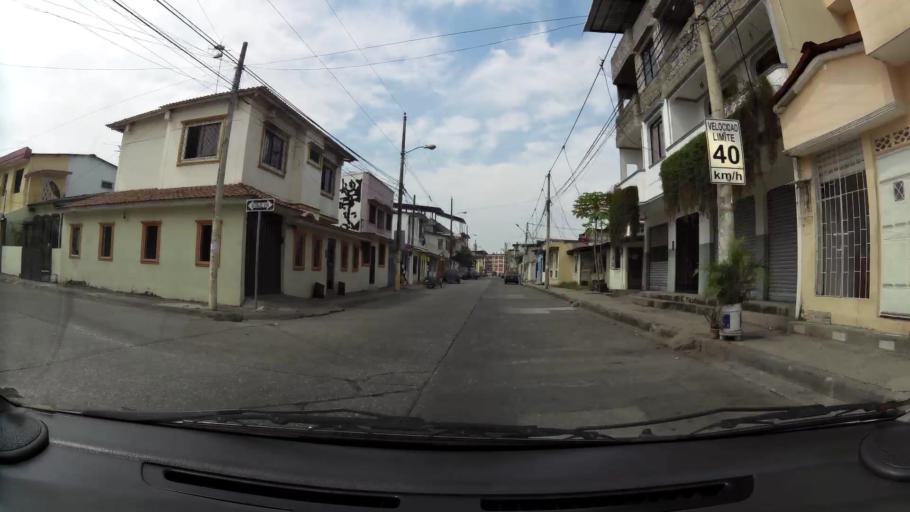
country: EC
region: Guayas
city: Eloy Alfaro
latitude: -2.1231
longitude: -79.8971
